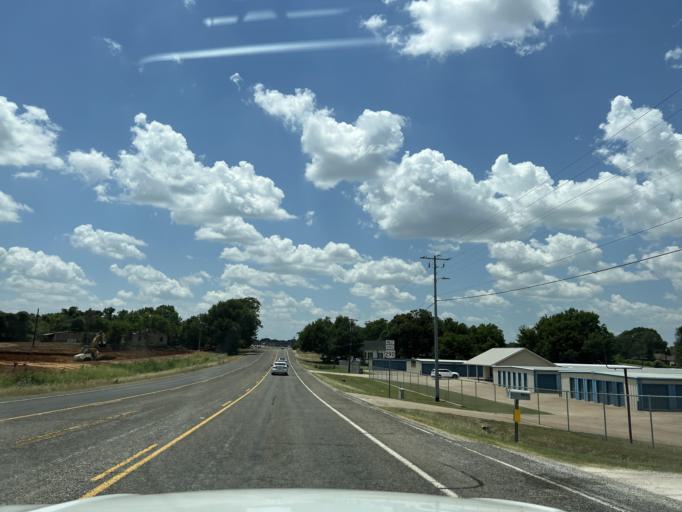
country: US
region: Texas
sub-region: Washington County
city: Brenham
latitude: 30.1472
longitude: -96.3778
